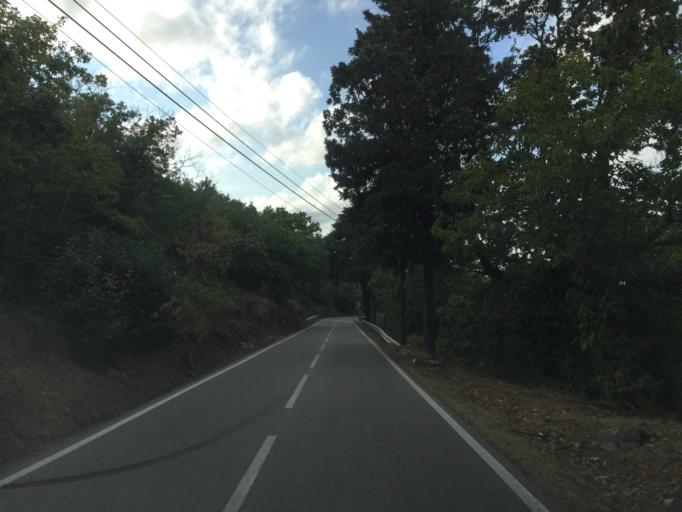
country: PT
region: Portalegre
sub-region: Marvao
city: Marvao
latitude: 39.3993
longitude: -7.3784
